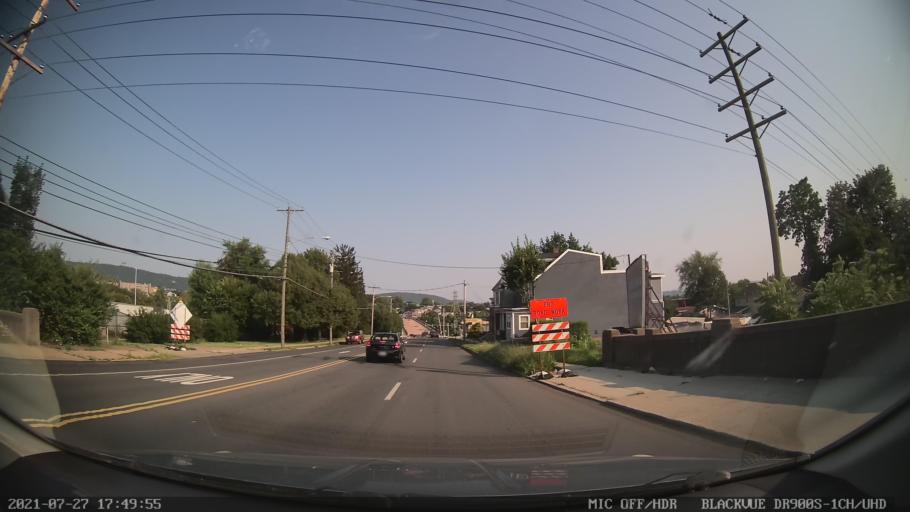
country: US
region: Pennsylvania
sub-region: Berks County
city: West Reading
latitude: 40.3532
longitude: -75.9463
